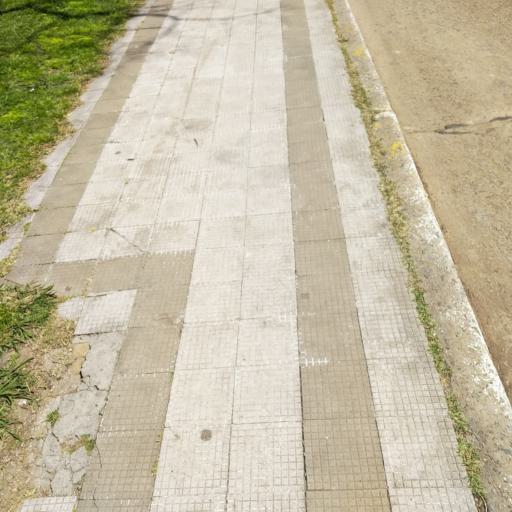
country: AR
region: Buenos Aires
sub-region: Partido de La Plata
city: La Plata
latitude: -34.8930
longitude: -57.9644
